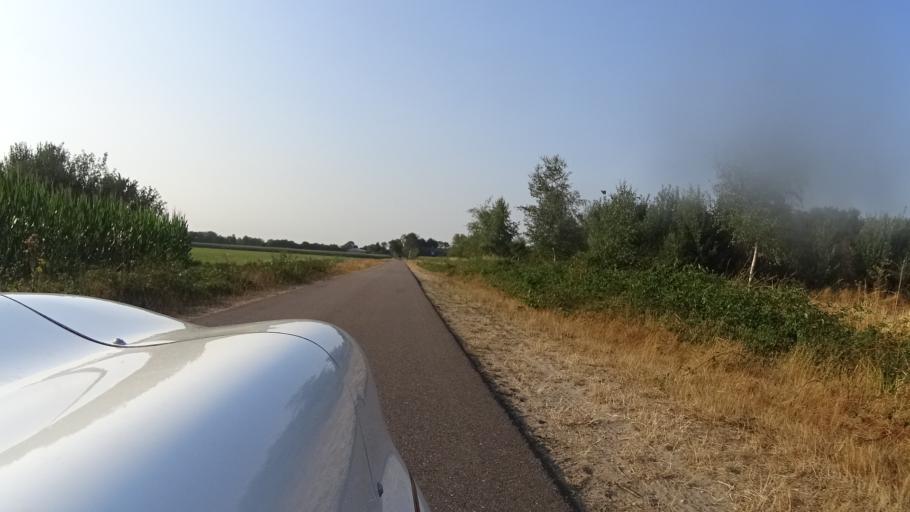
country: NL
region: North Brabant
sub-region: Gemeente Landerd
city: Zeeland
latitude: 51.7143
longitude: 5.6734
